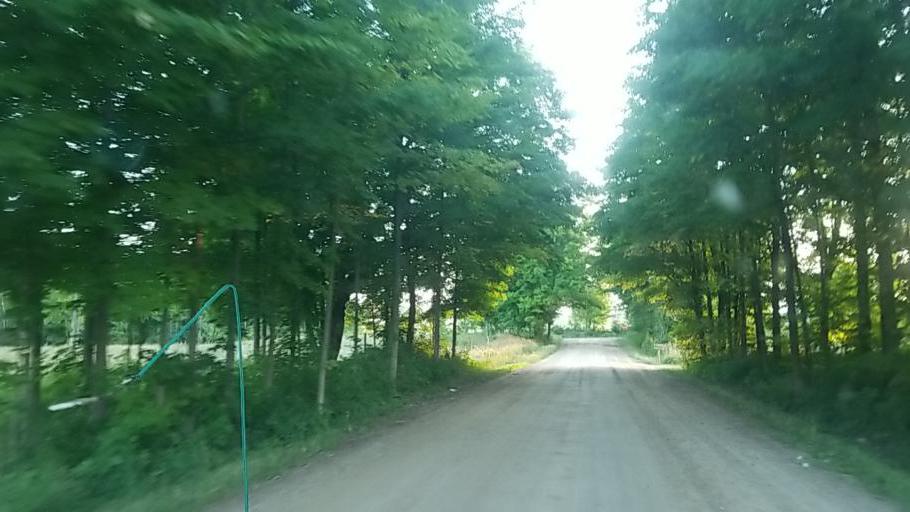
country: US
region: Michigan
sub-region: Osceola County
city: Evart
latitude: 43.9139
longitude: -85.2066
